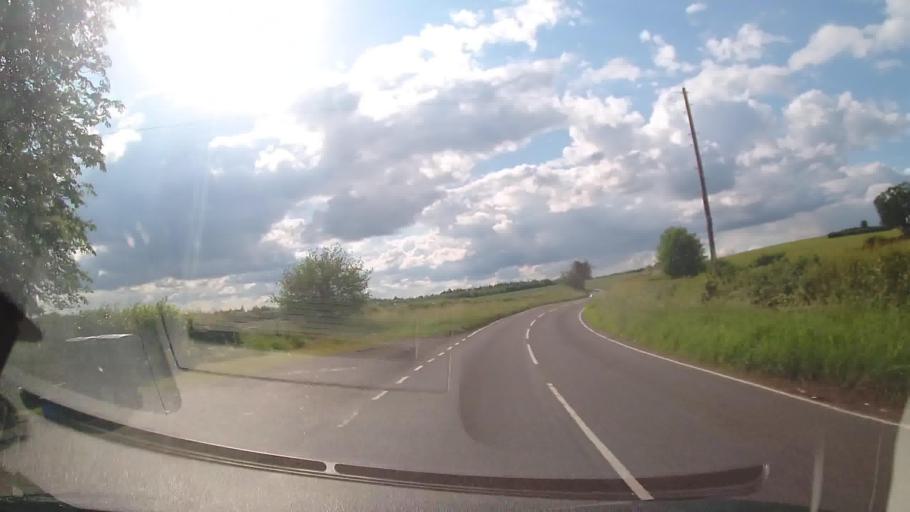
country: GB
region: England
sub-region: Shropshire
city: Harley
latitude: 52.6495
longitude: -2.6041
